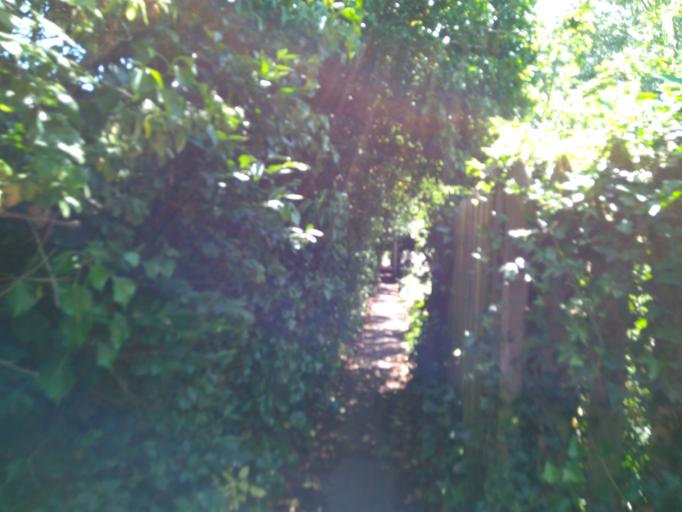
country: GB
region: England
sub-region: Kent
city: Whitstable
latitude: 51.3515
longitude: 1.0188
